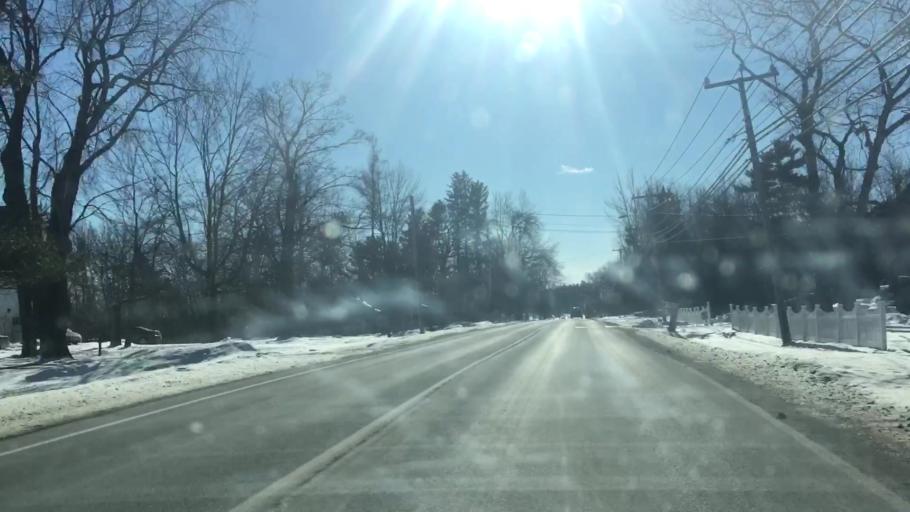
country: US
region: Maine
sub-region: Hancock County
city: Ellsworth
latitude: 44.5346
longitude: -68.4311
